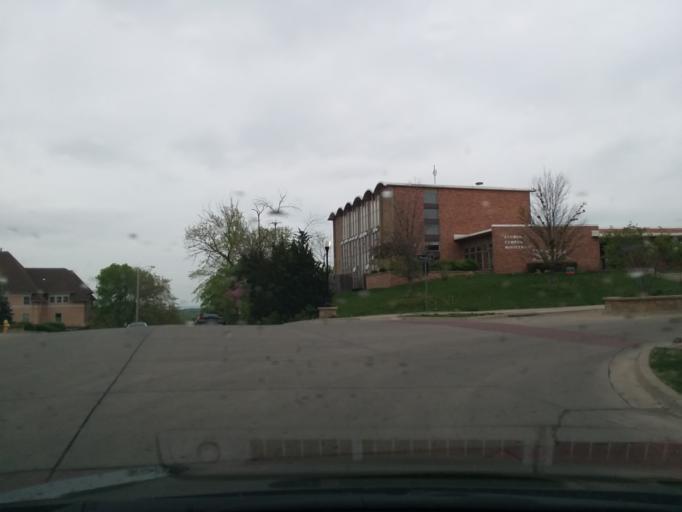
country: US
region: Kansas
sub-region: Douglas County
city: Lawrence
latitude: 38.9619
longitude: -95.2428
